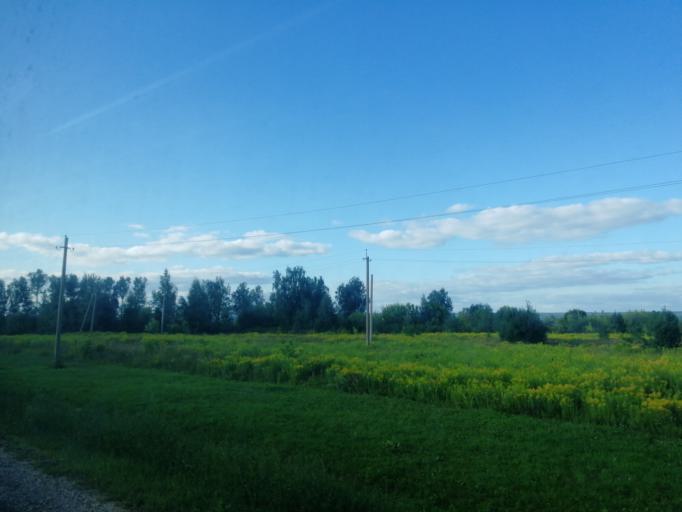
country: RU
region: Tula
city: Leninskiy
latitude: 54.2465
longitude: 37.3249
